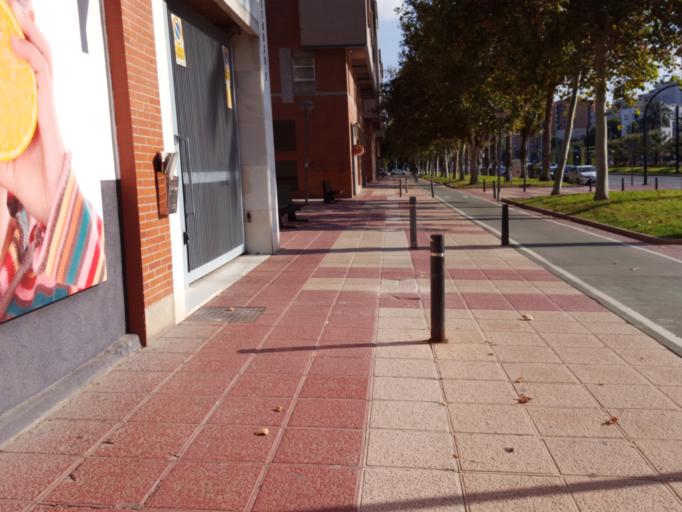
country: ES
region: Murcia
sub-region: Murcia
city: Murcia
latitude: 37.9953
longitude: -1.1247
